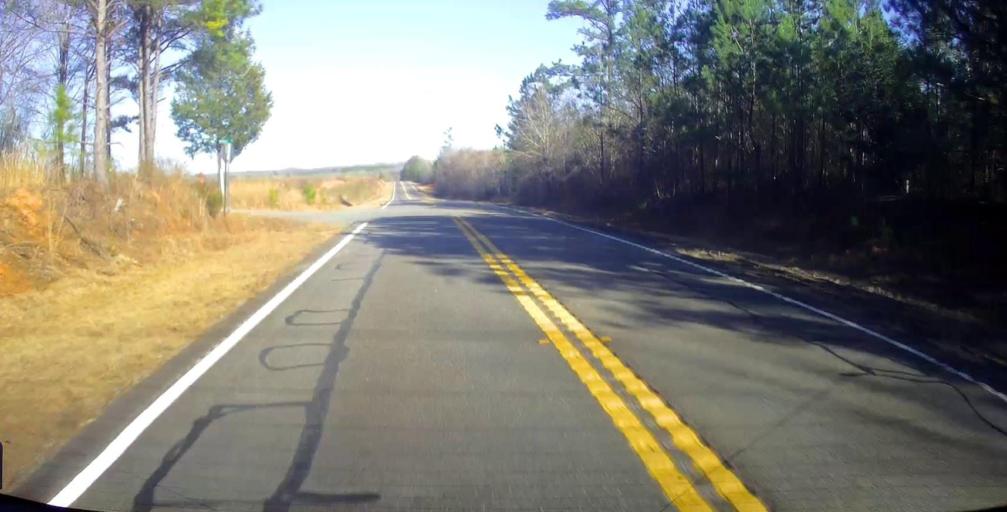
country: US
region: Georgia
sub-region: Talbot County
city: Talbotton
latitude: 32.6722
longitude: -84.4813
